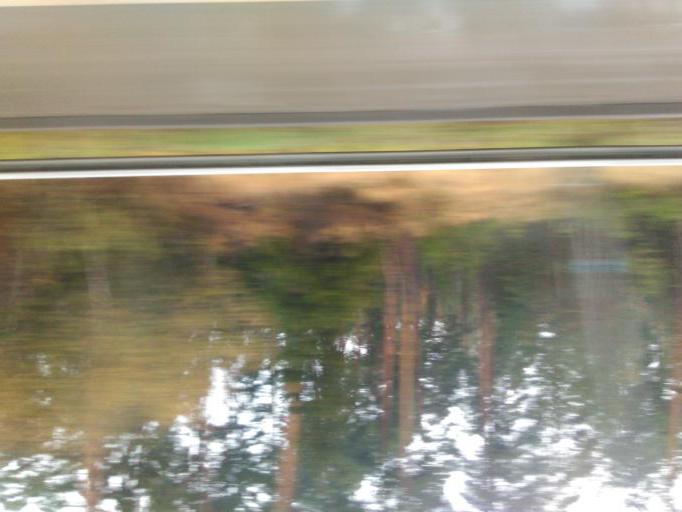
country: RU
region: Tatarstan
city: Osinovo
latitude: 55.8285
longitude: 48.8486
